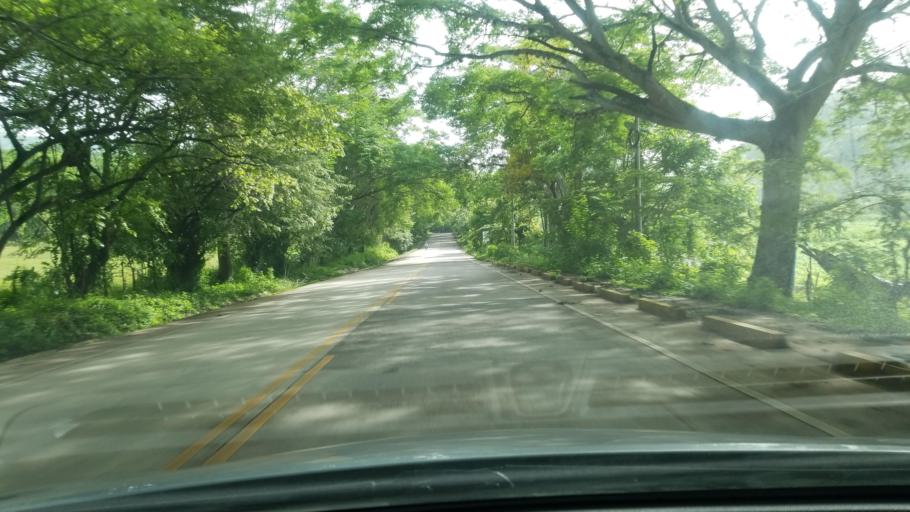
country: HN
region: Copan
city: Copan
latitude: 14.8493
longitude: -89.1321
